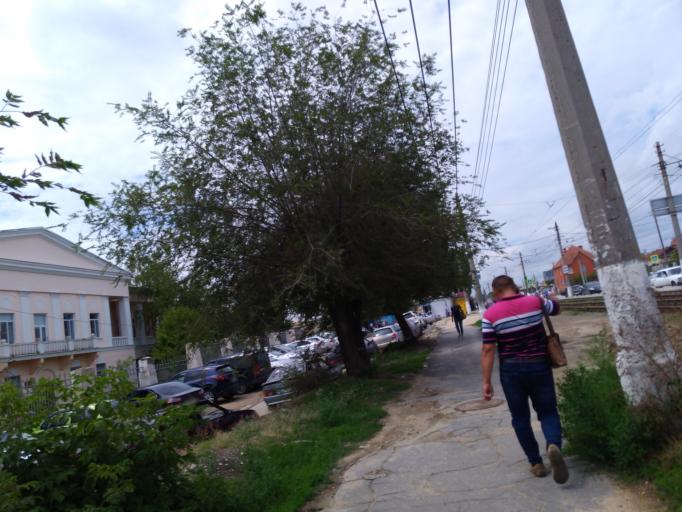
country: RU
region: Volgograd
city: Volgograd
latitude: 48.7152
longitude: 44.4916
